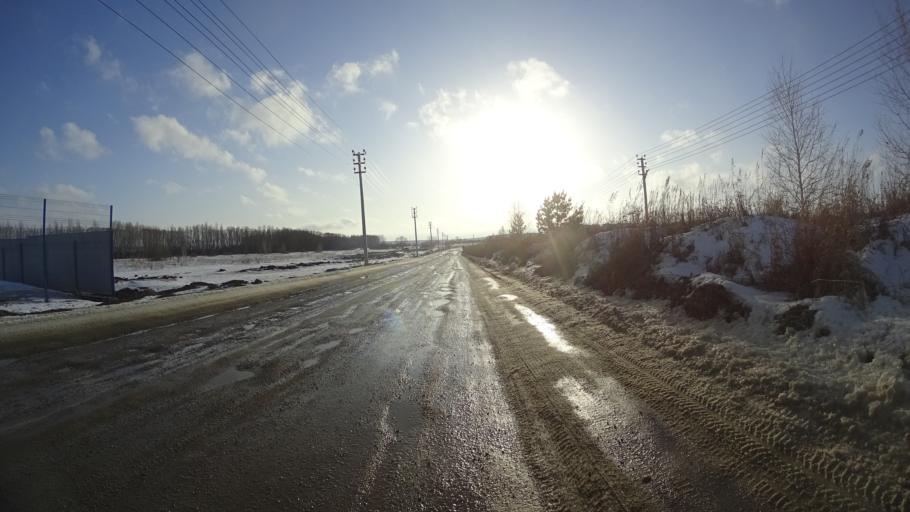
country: RU
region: Chelyabinsk
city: Sargazy
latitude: 55.1072
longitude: 61.2695
